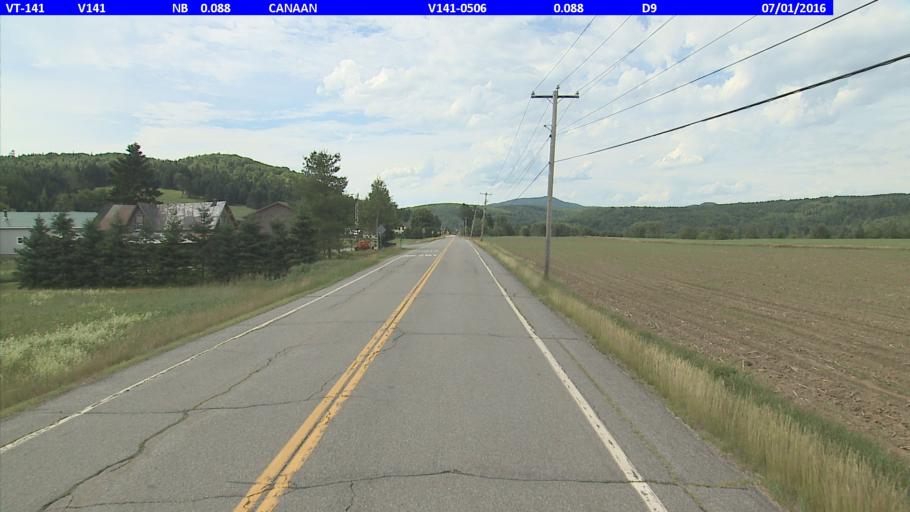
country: US
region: New Hampshire
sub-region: Coos County
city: Colebrook
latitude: 45.0081
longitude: -71.5566
